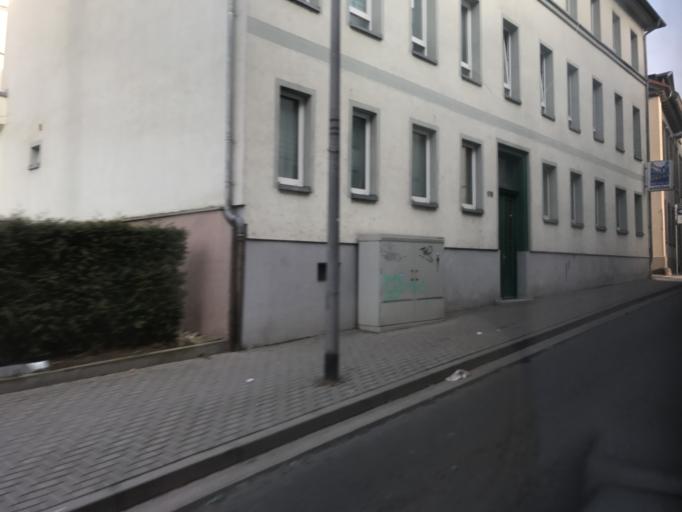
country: DE
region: Hesse
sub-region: Regierungsbezirk Darmstadt
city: Wiesbaden
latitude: 50.0356
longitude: 8.2392
